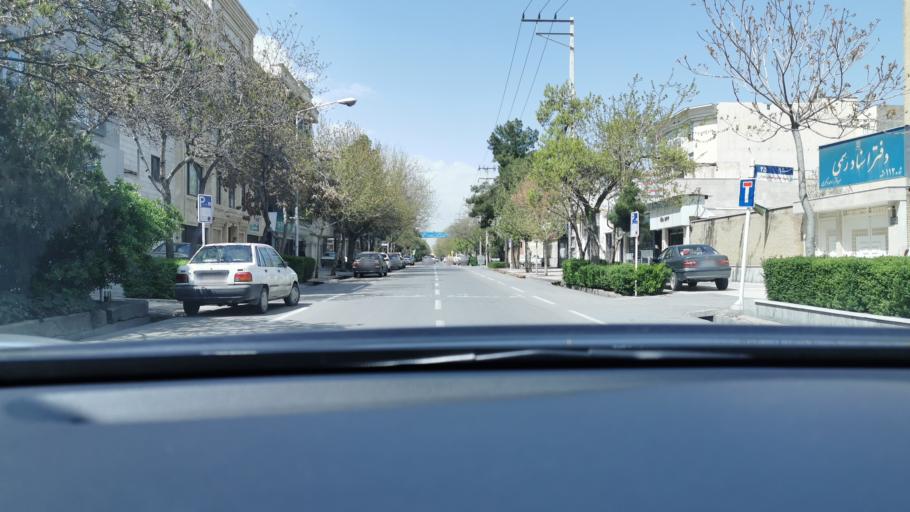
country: IR
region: Razavi Khorasan
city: Mashhad
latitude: 36.2988
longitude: 59.5907
